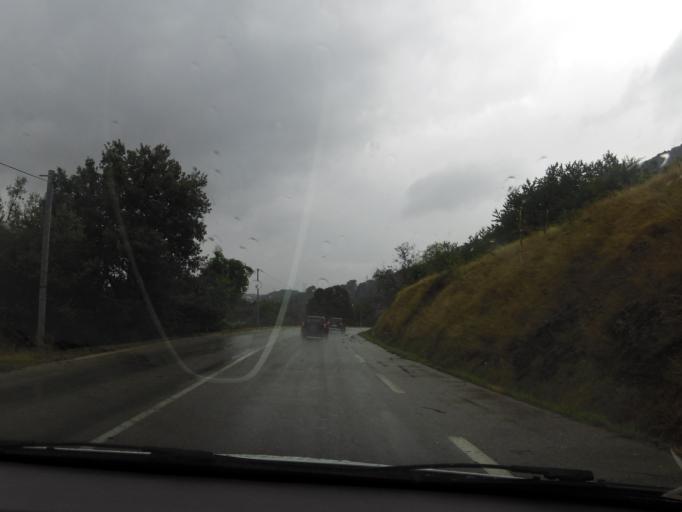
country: FR
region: Languedoc-Roussillon
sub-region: Departement du Gard
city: Les Salles-du-Gardon
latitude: 44.1965
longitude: 4.0442
